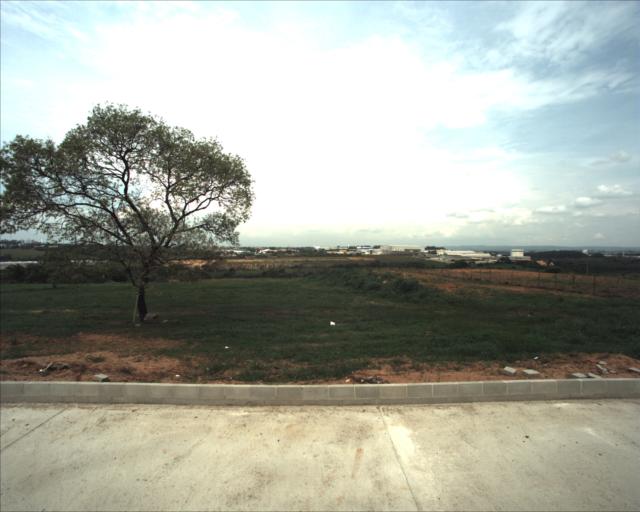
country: BR
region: Sao Paulo
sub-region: Sorocaba
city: Sorocaba
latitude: -23.4465
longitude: -47.4393
